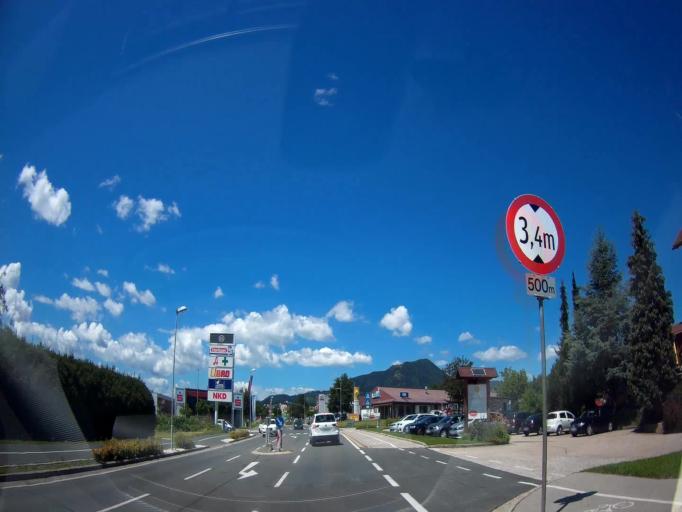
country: AT
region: Carinthia
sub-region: Politischer Bezirk Sankt Veit an der Glan
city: Sankt Veit an der Glan
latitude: 46.7662
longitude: 14.3735
